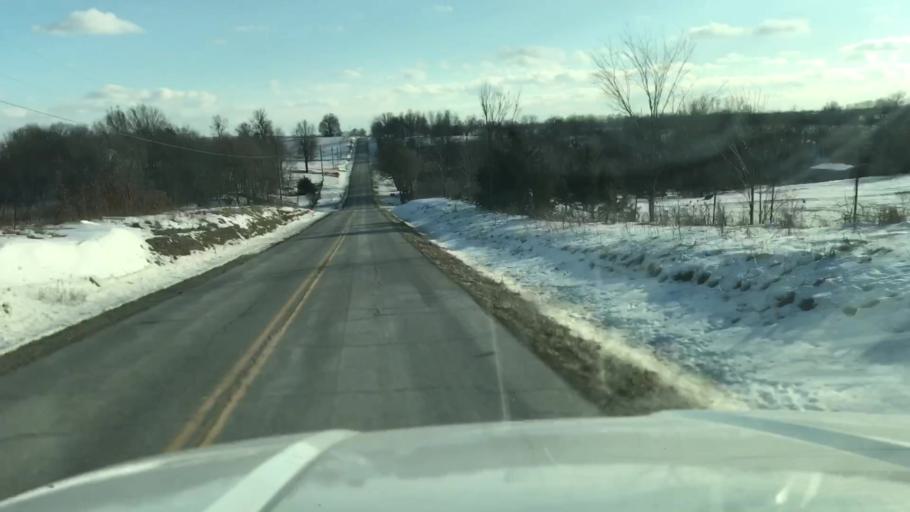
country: US
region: Missouri
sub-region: Holt County
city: Oregon
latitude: 40.0614
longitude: -94.9749
